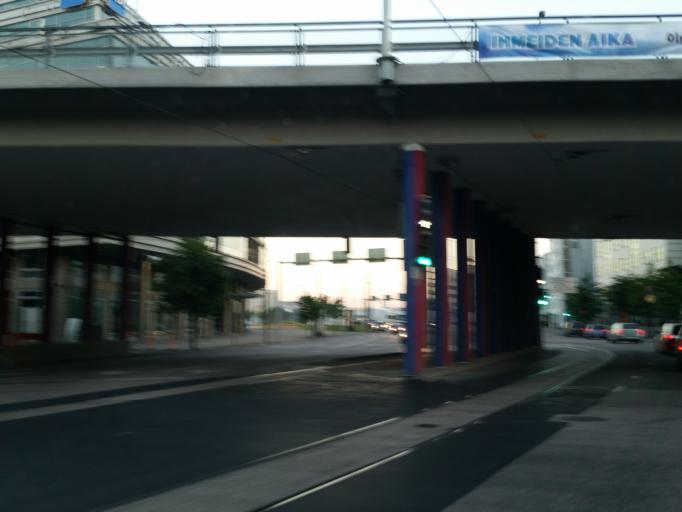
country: FI
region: Uusimaa
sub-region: Helsinki
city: Helsinki
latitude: 60.1649
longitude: 24.9211
